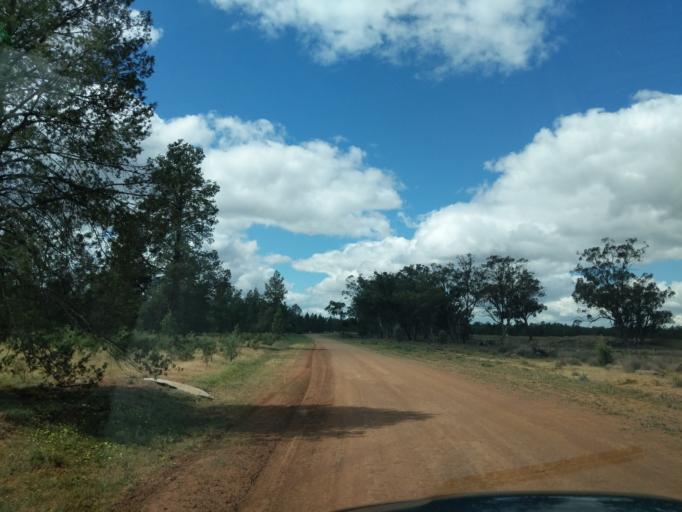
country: AU
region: New South Wales
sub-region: Coolamon
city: Coolamon
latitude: -34.8552
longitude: 146.9110
